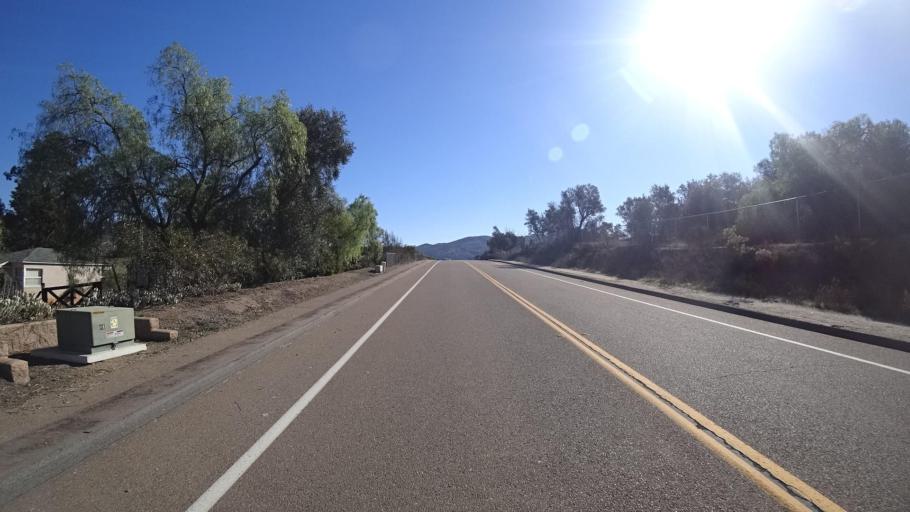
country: US
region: California
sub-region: San Diego County
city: Jamul
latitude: 32.7222
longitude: -116.8646
